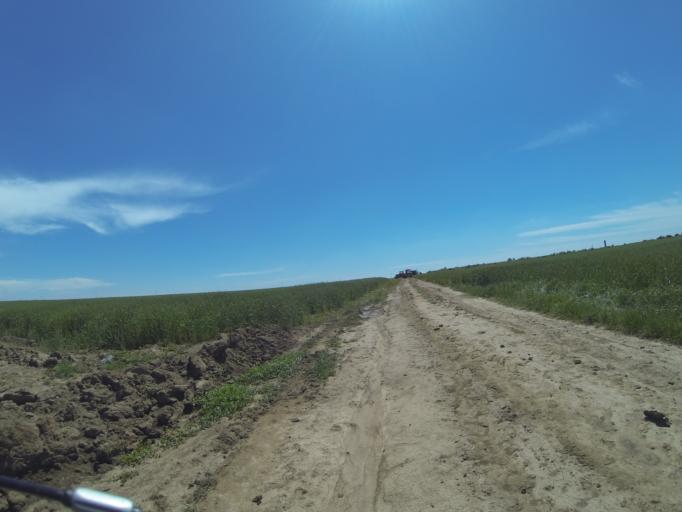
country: RO
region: Dolj
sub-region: Comuna Dragotesti
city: Dragotesti
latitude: 44.2045
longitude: 24.0668
